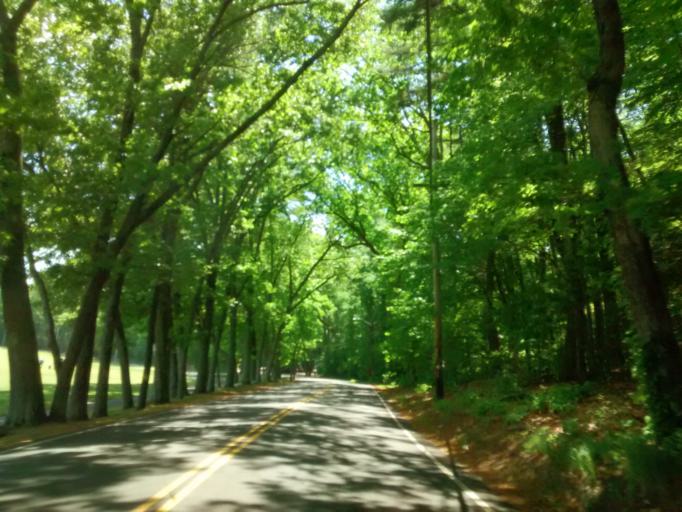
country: US
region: Massachusetts
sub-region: Worcester County
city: Whitinsville
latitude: 42.1041
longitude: -71.6597
